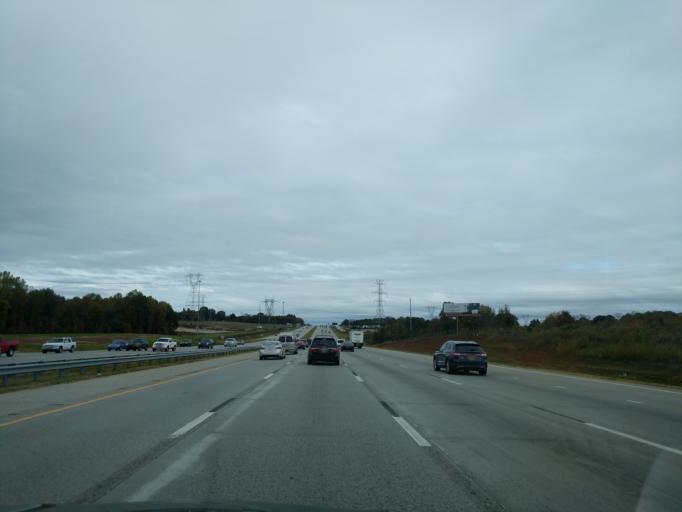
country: US
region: North Carolina
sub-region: Rowan County
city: Spencer
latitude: 35.7316
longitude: -80.3760
